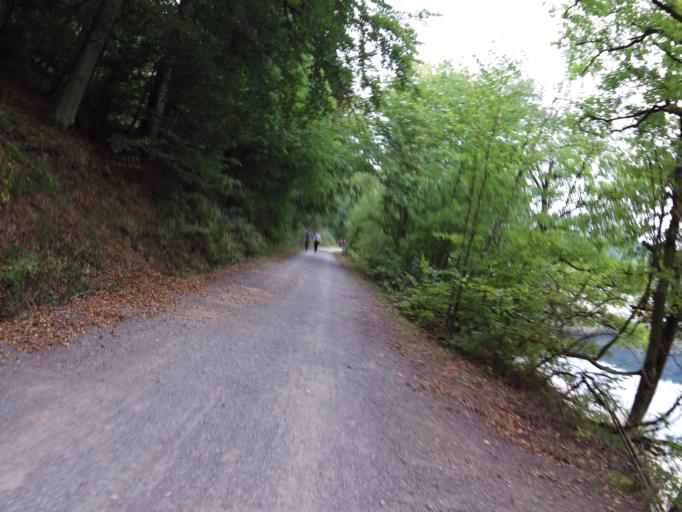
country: DE
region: North Rhine-Westphalia
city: Heimbach
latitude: 50.6112
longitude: 6.3934
